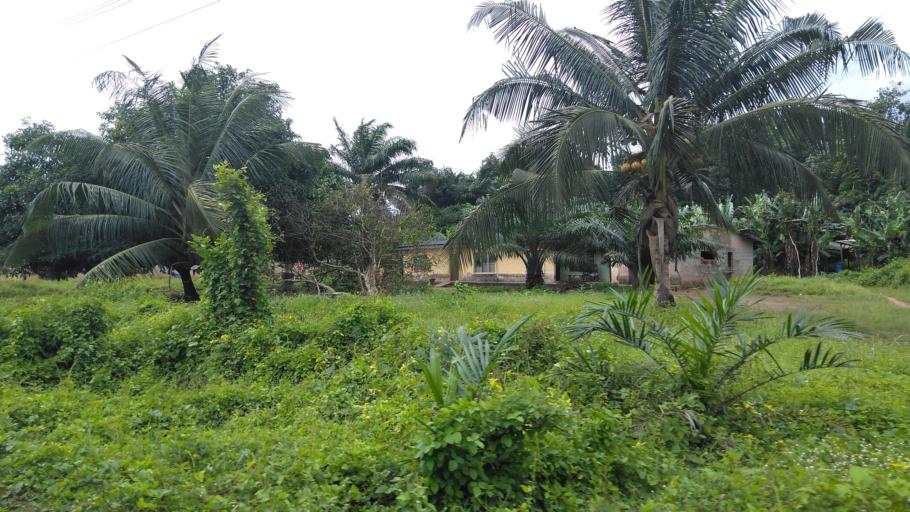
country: NG
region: Ogun
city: Abigi
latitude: 6.6046
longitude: 4.4881
